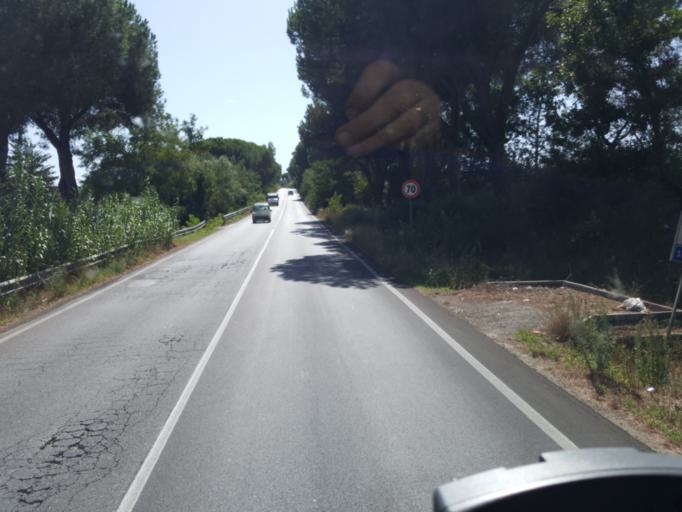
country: IT
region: Latium
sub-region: Provincia di Latina
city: Genio Civile
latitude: 41.5339
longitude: 12.7117
